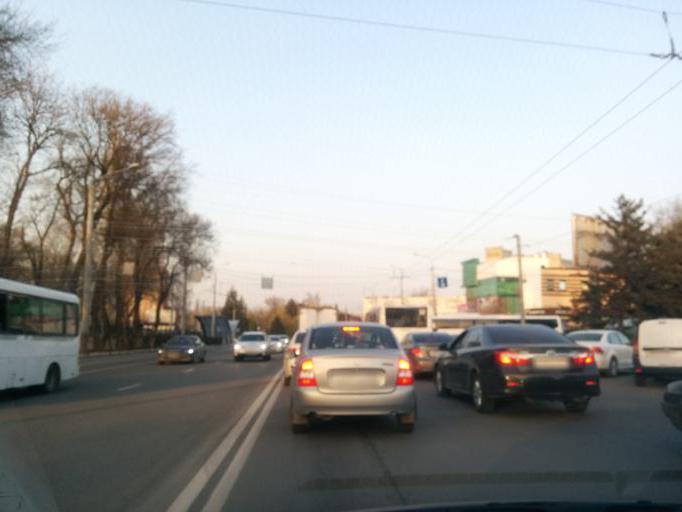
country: RU
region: Rostov
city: Rostov-na-Donu
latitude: 47.2422
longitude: 39.7631
